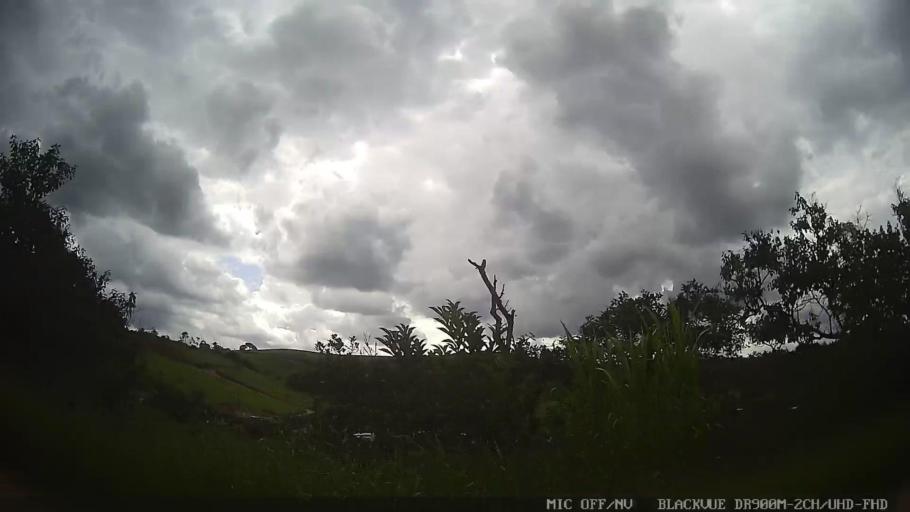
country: BR
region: Sao Paulo
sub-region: Ribeirao Pires
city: Ribeirao Pires
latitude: -23.6568
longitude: -46.3135
